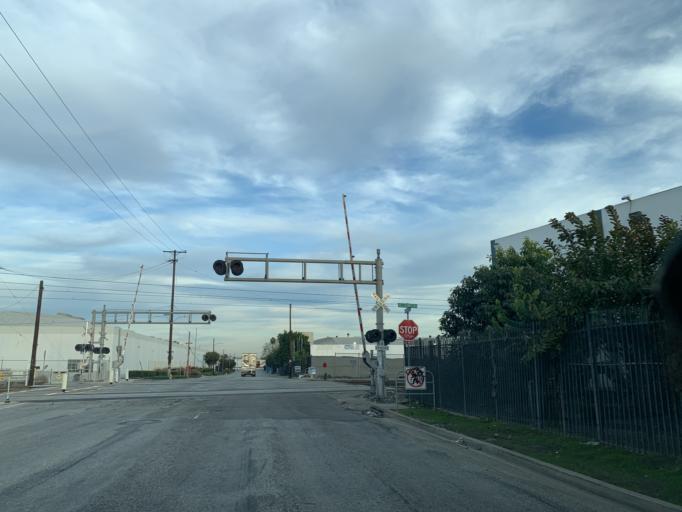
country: US
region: California
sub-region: Los Angeles County
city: Compton
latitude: 33.8704
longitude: -118.2208
